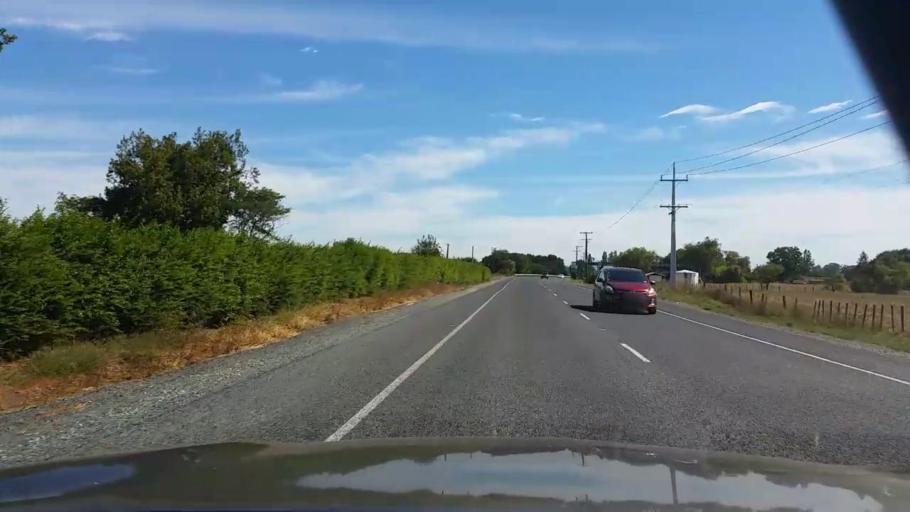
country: NZ
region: Waikato
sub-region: Hamilton City
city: Hamilton
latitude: -37.6675
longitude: 175.3007
